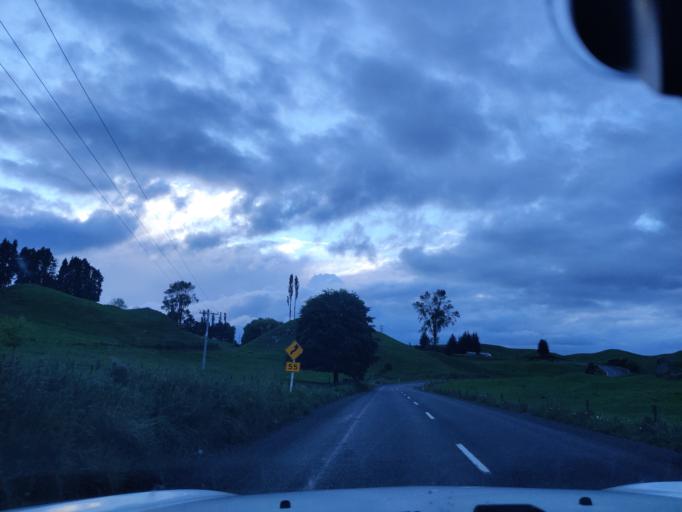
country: NZ
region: Waikato
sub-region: South Waikato District
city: Tokoroa
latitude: -38.2012
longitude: 175.8112
